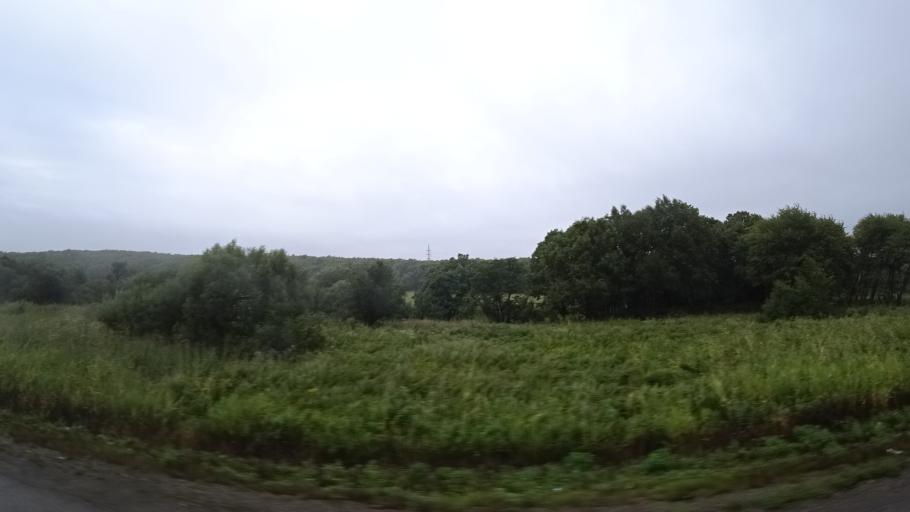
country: RU
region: Primorskiy
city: Monastyrishche
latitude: 44.2758
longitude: 132.4815
